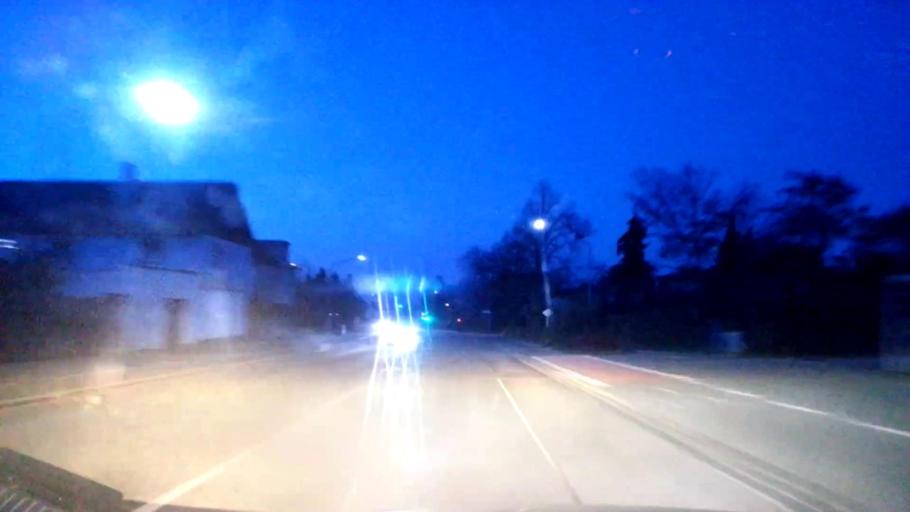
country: DE
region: Bavaria
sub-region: Upper Franconia
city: Bamberg
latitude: 49.8782
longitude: 10.8841
